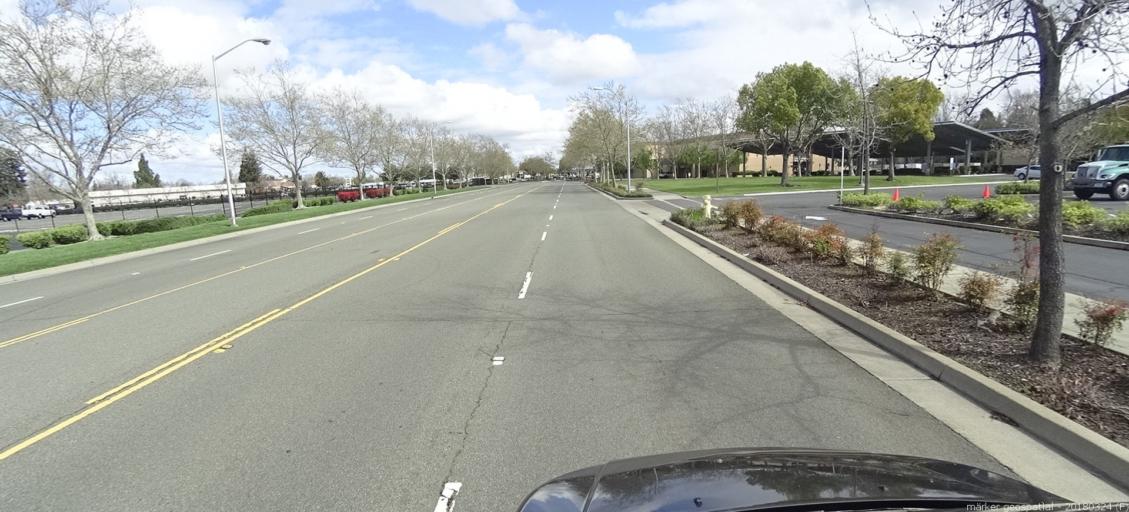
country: US
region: California
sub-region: Sacramento County
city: North Highlands
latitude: 38.6630
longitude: -121.3877
